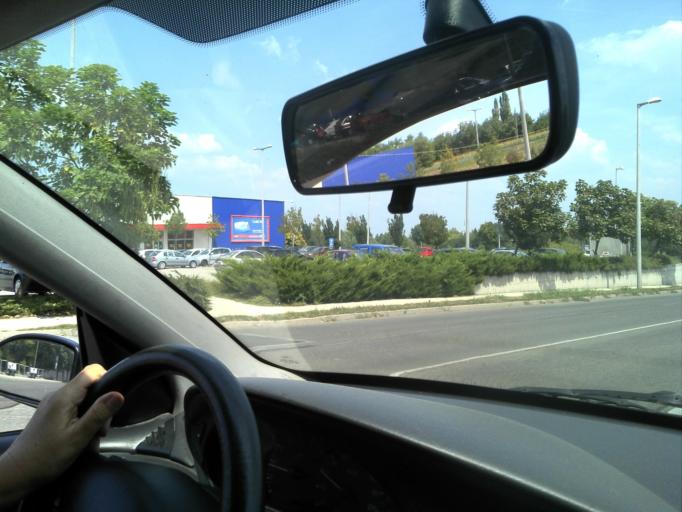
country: HU
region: Tolna
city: Dombovar
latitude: 46.3859
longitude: 18.1377
